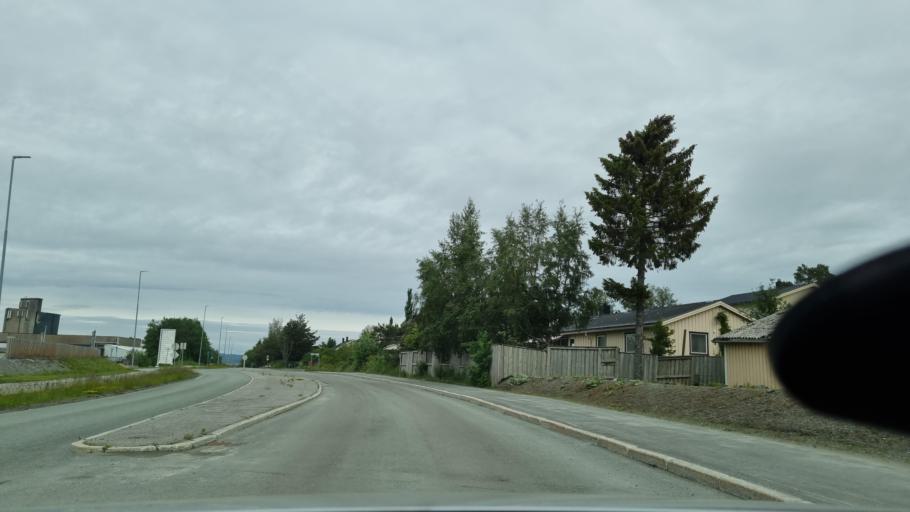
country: NO
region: Sor-Trondelag
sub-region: Trondheim
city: Trondheim
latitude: 63.3399
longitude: 10.3615
